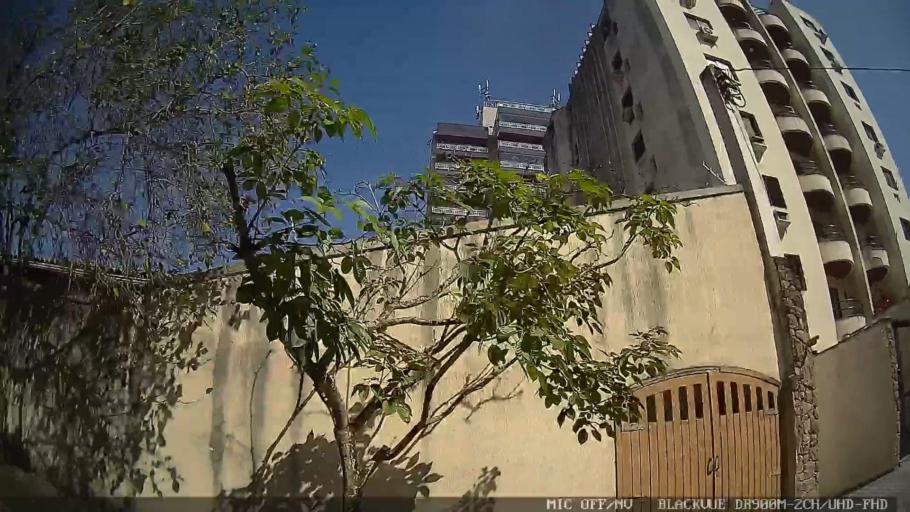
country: BR
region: Sao Paulo
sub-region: Guaruja
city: Guaruja
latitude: -24.0124
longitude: -46.2766
